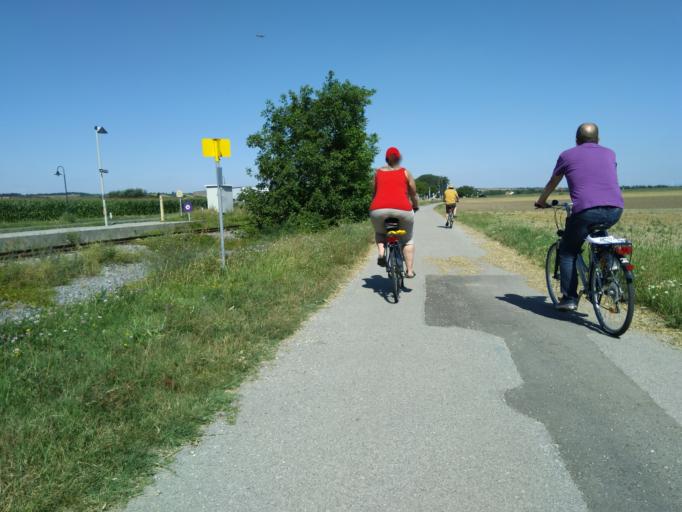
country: AT
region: Lower Austria
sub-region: Politischer Bezirk Mistelbach
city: Pillichsdorf
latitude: 48.3623
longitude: 16.5177
